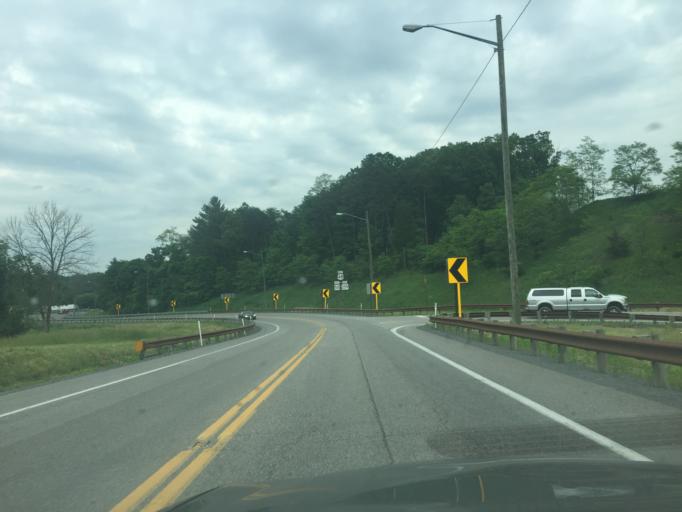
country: US
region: Virginia
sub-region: Shenandoah County
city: Woodstock
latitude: 39.0757
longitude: -78.6232
